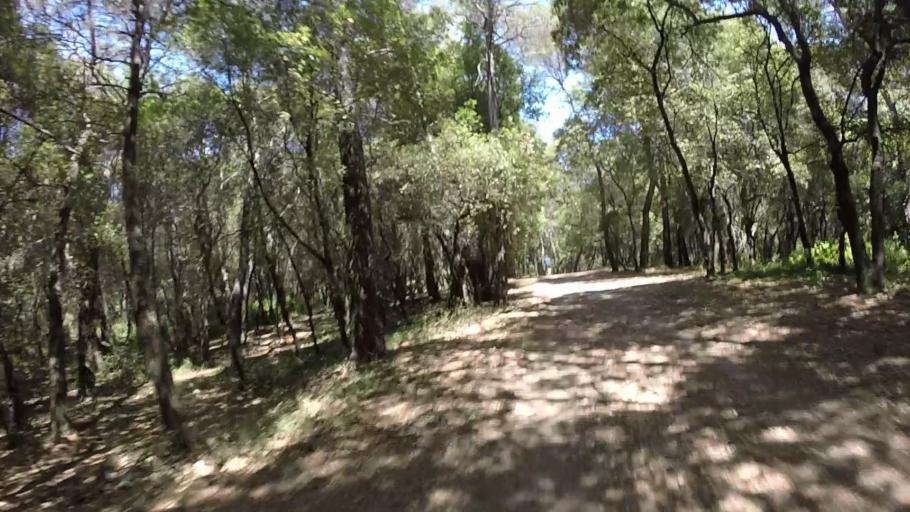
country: FR
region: Provence-Alpes-Cote d'Azur
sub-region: Departement des Alpes-Maritimes
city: Mougins
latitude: 43.5961
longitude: 7.0226
